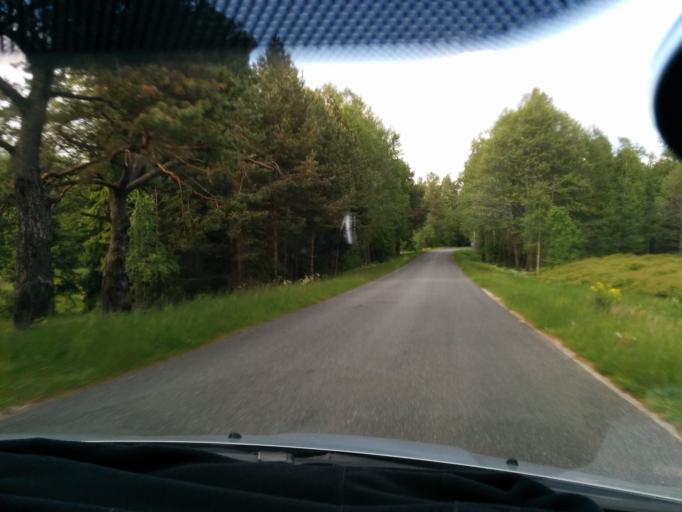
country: EE
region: Harju
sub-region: Loksa linn
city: Loksa
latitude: 59.6352
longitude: 25.6857
